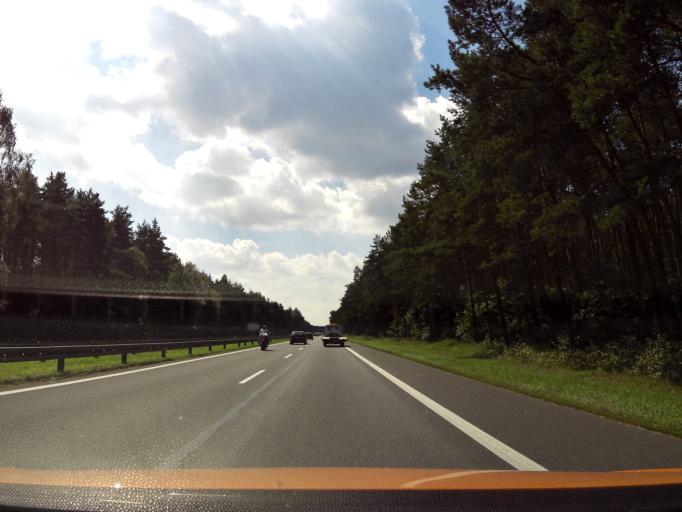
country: PL
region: West Pomeranian Voivodeship
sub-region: Powiat stargardzki
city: Kobylanka
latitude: 53.4339
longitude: 14.7754
